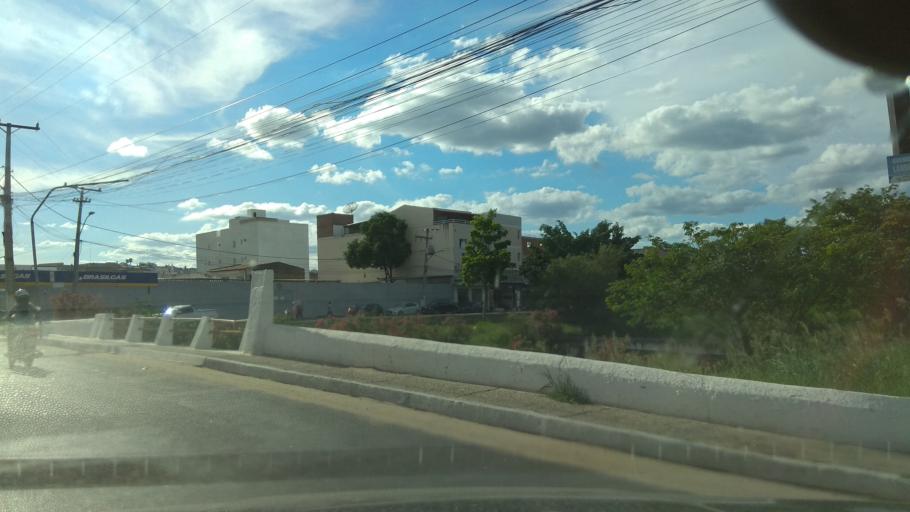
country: BR
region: Bahia
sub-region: Jequie
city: Jequie
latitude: -13.8647
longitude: -40.0772
